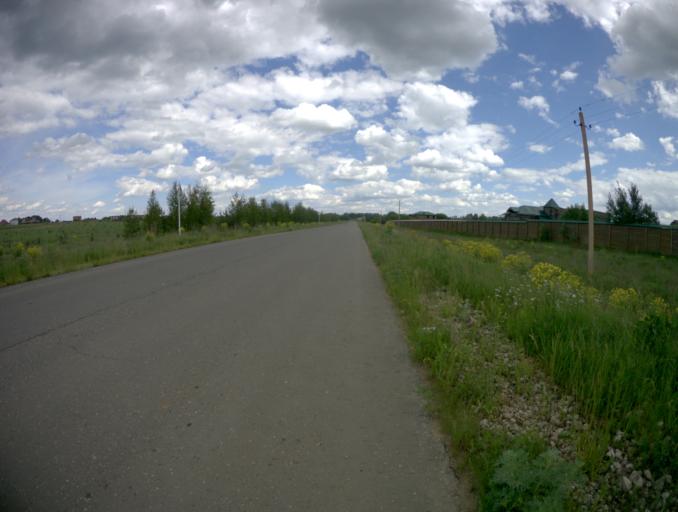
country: RU
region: Vladimir
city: Suzdal'
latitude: 56.4429
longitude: 40.4255
